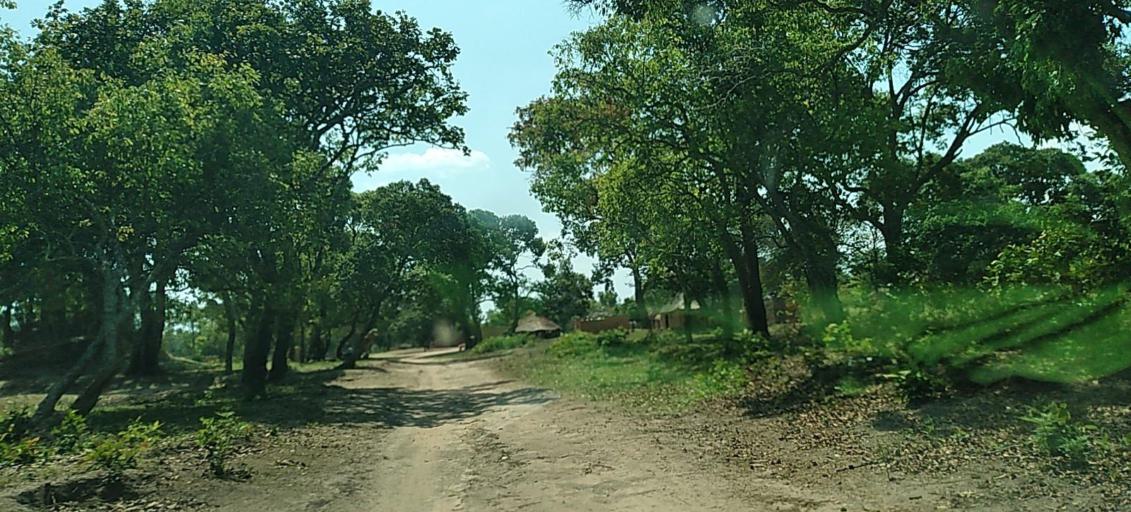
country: CD
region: Katanga
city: Kolwezi
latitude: -11.2757
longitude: 25.1102
